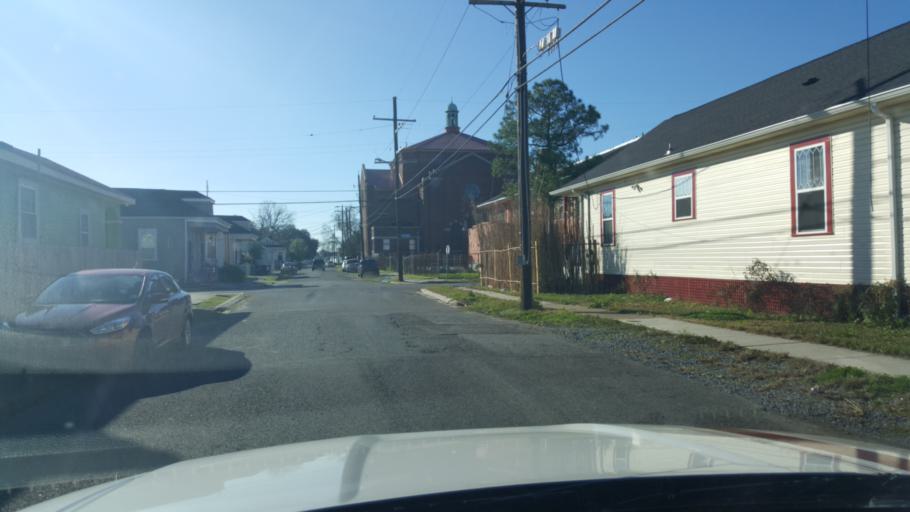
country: US
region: Louisiana
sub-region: Orleans Parish
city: New Orleans
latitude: 29.9784
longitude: -90.0518
